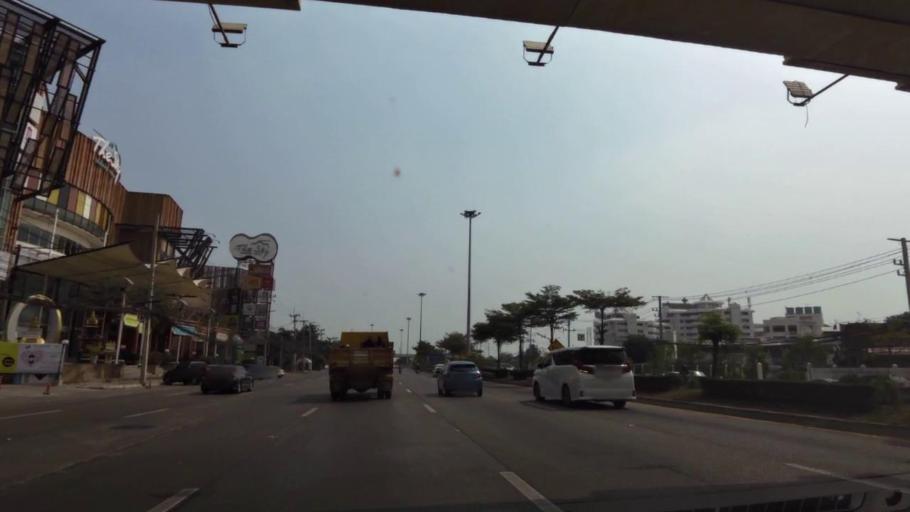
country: TH
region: Phra Nakhon Si Ayutthaya
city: Phra Nakhon Si Ayutthaya
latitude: 14.3451
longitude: 100.6085
